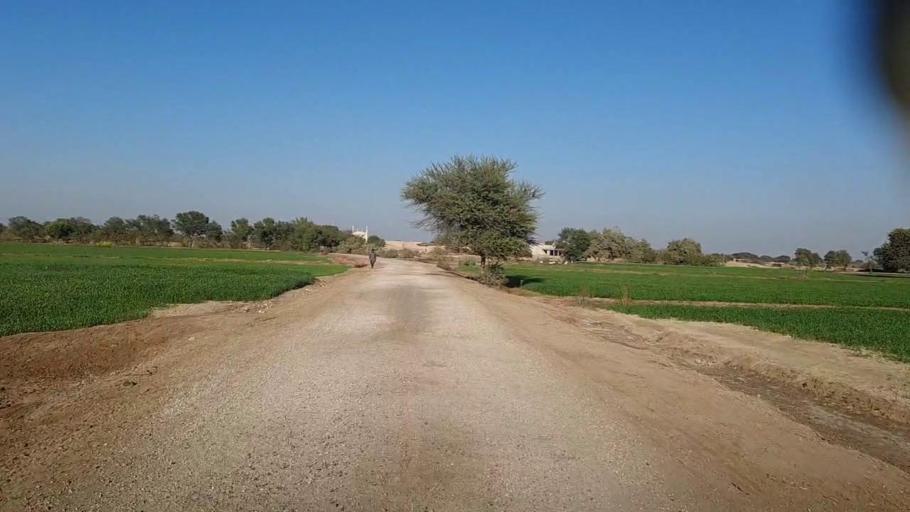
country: PK
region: Sindh
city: Khairpur
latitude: 27.8912
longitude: 69.7522
